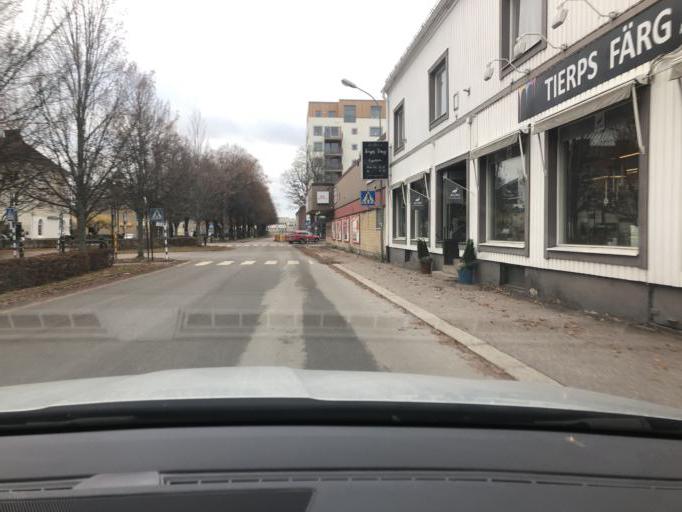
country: SE
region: Uppsala
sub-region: Tierps Kommun
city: Tierp
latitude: 60.3440
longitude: 17.5158
